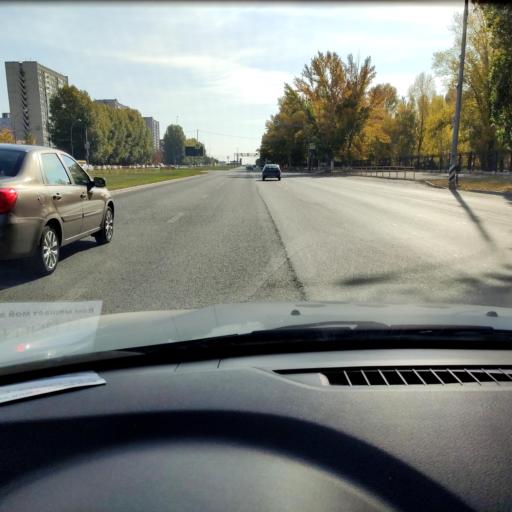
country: RU
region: Samara
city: Tol'yatti
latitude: 53.5102
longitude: 49.2767
